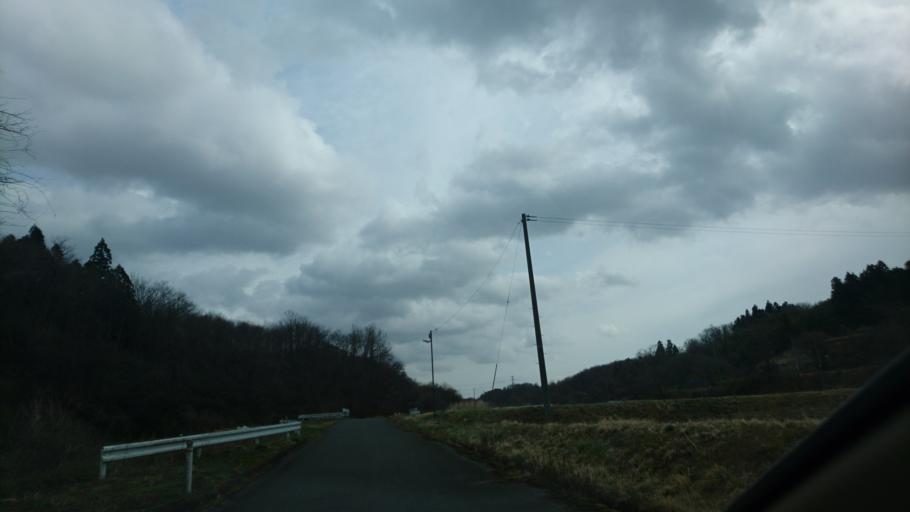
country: JP
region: Iwate
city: Ichinoseki
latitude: 38.8966
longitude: 141.1829
